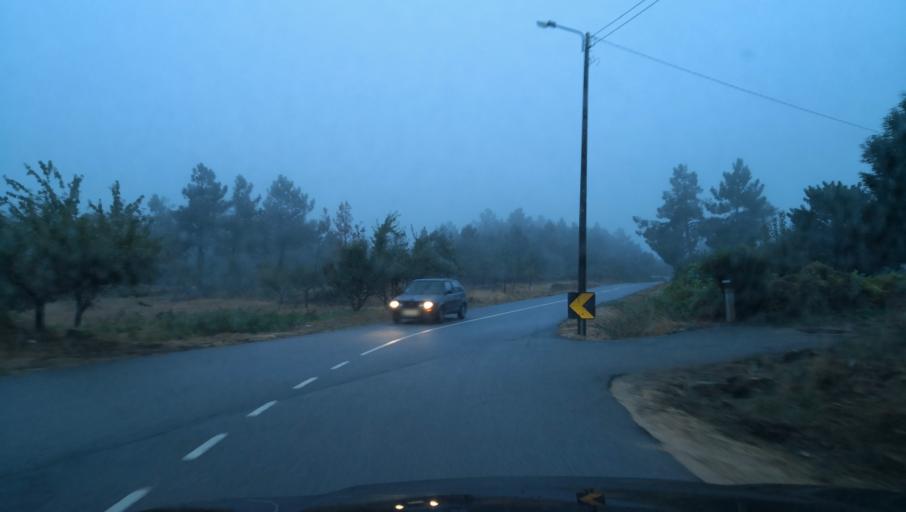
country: PT
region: Vila Real
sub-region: Sabrosa
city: Sabrosa
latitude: 41.2811
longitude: -7.5966
